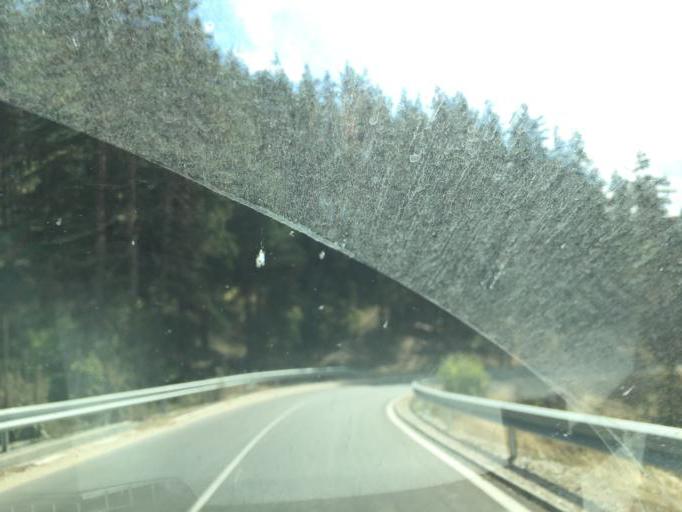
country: BG
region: Pazardzhik
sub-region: Obshtina Batak
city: Batak
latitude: 41.8899
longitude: 24.3327
